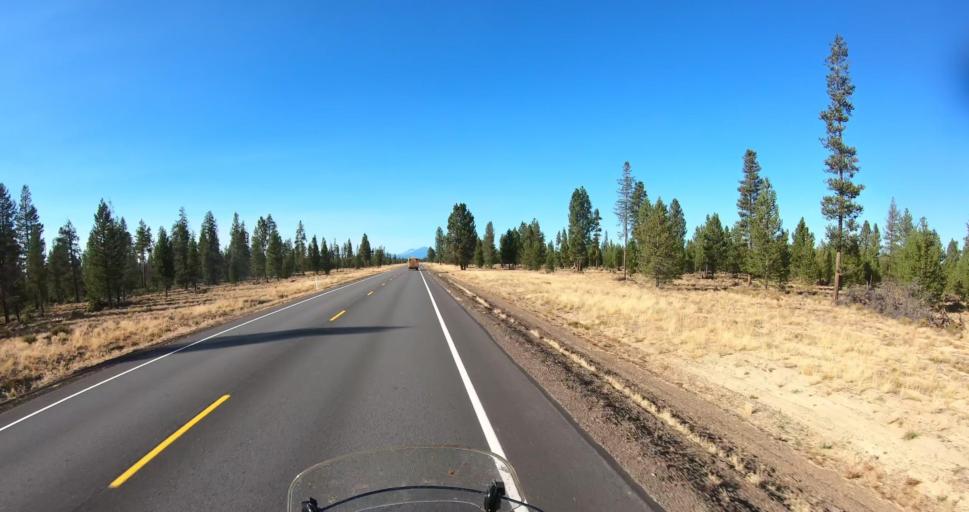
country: US
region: Oregon
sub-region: Deschutes County
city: La Pine
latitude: 43.5986
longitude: -121.4968
